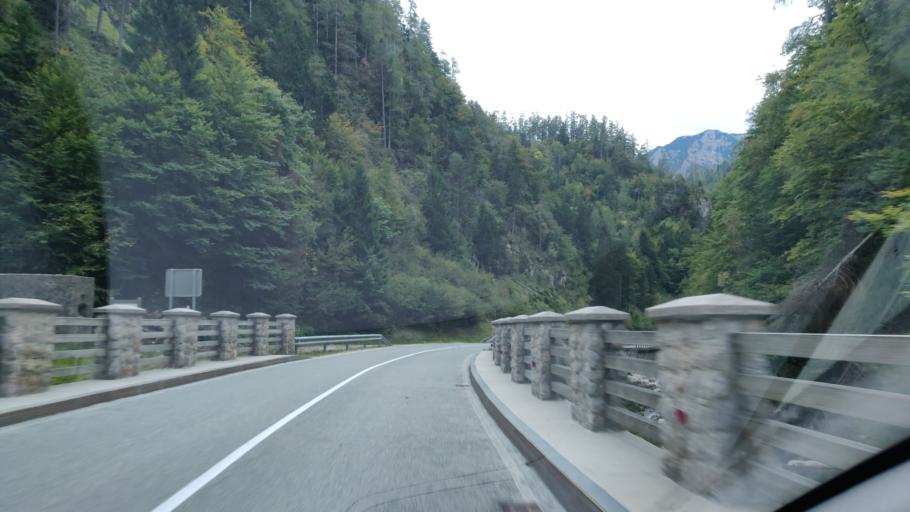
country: SI
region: Jezersko
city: Zgornje Jezersko
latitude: 46.3747
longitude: 14.4717
